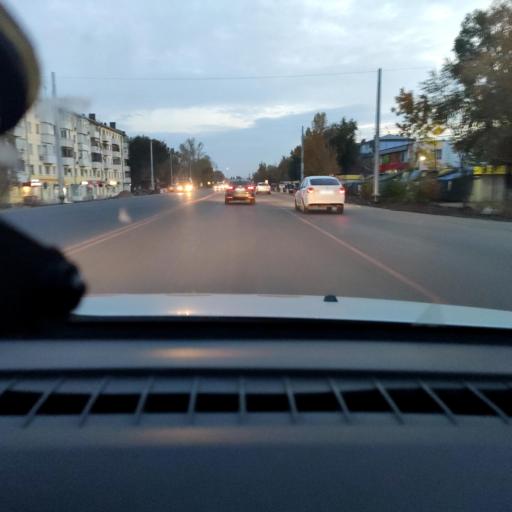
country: RU
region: Samara
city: Samara
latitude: 53.1206
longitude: 50.0870
